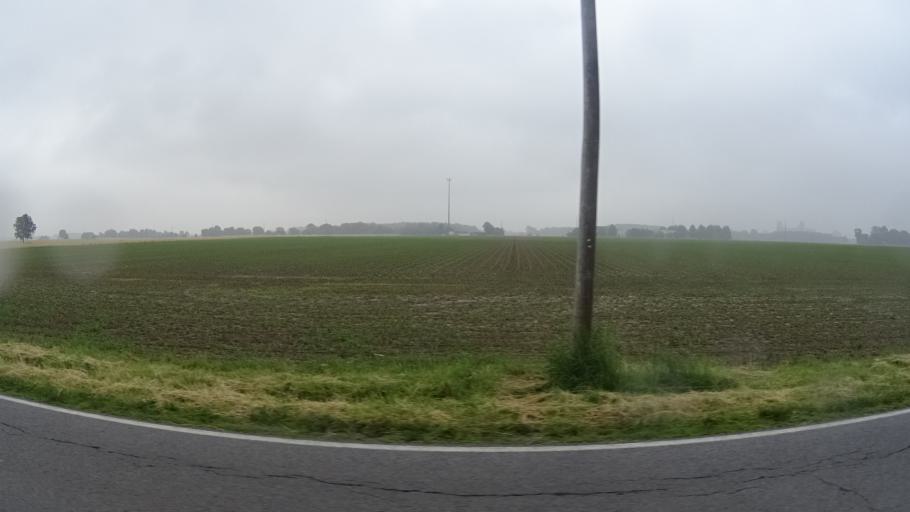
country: US
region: Ohio
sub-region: Huron County
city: Bellevue
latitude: 41.2948
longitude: -82.8417
